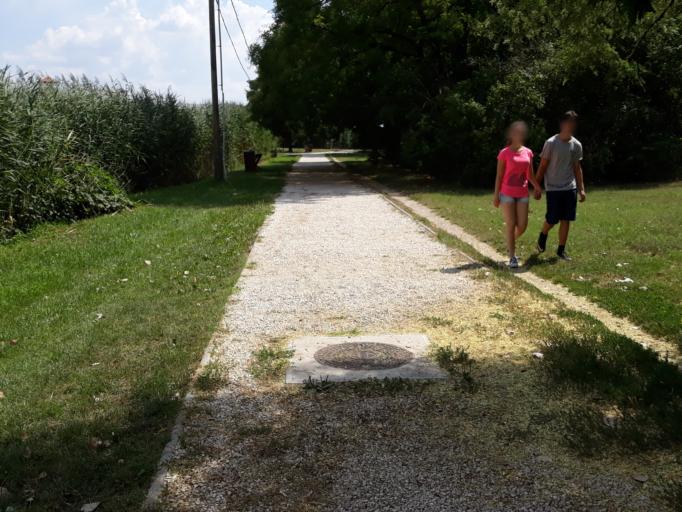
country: HU
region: Bekes
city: Oroshaza
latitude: 46.5691
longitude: 20.6255
